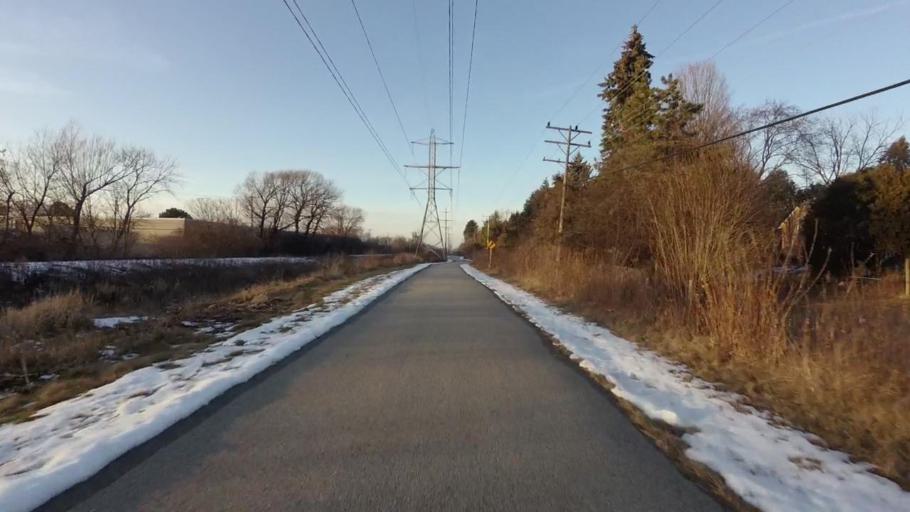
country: US
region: Wisconsin
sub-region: Milwaukee County
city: Brown Deer
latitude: 43.1646
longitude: -87.9614
